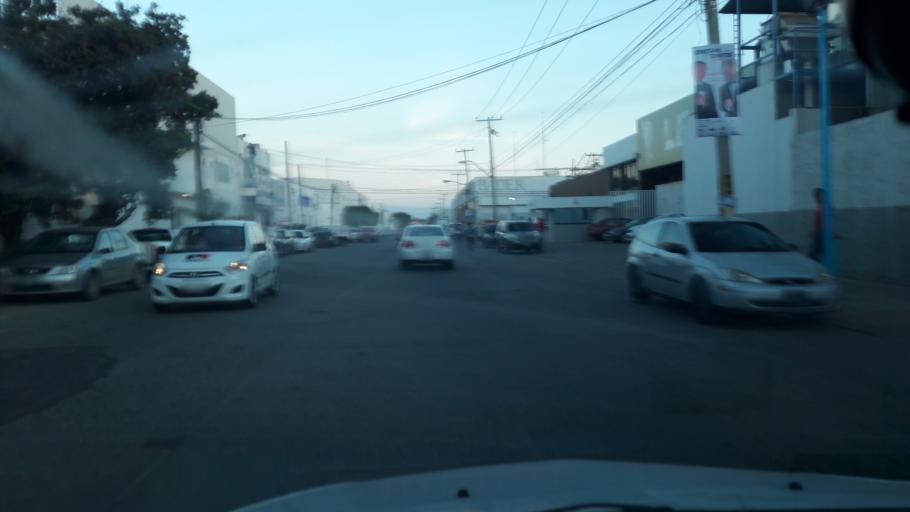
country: MX
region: Guanajuato
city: Leon
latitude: 21.1655
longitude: -101.6731
